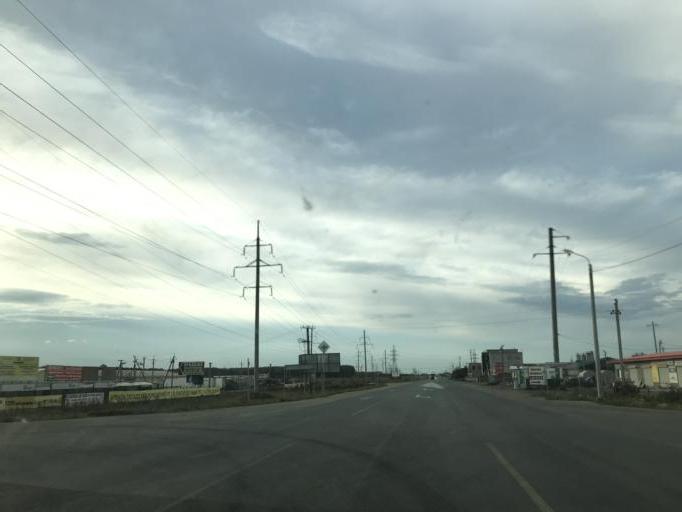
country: RU
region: Chelyabinsk
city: Roshchino
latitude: 55.2327
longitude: 61.2824
